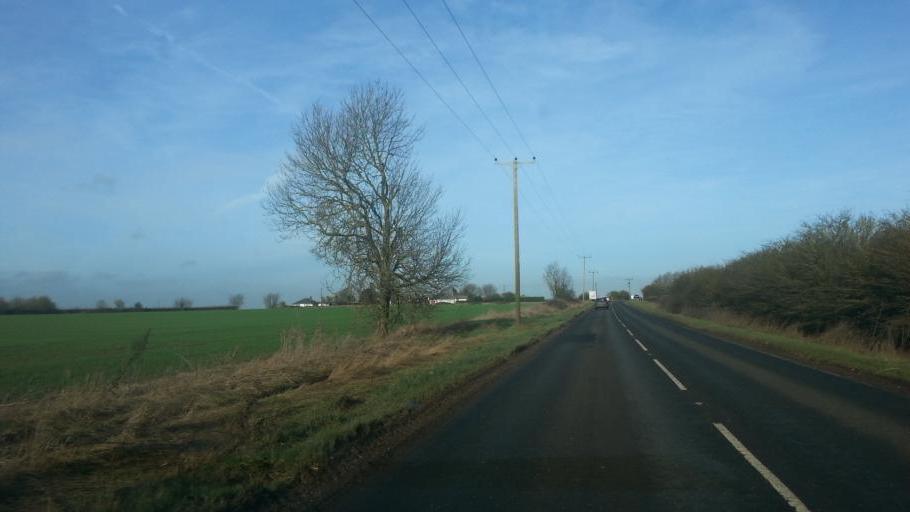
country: GB
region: England
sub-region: Cambridgeshire
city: Warboys
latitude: 52.4134
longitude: -0.1046
